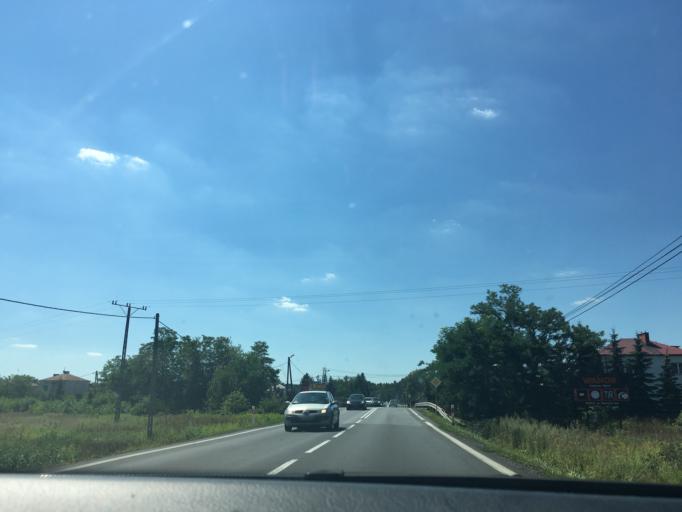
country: PL
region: Subcarpathian Voivodeship
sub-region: Powiat nizanski
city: Nisko
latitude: 50.5025
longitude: 22.1400
